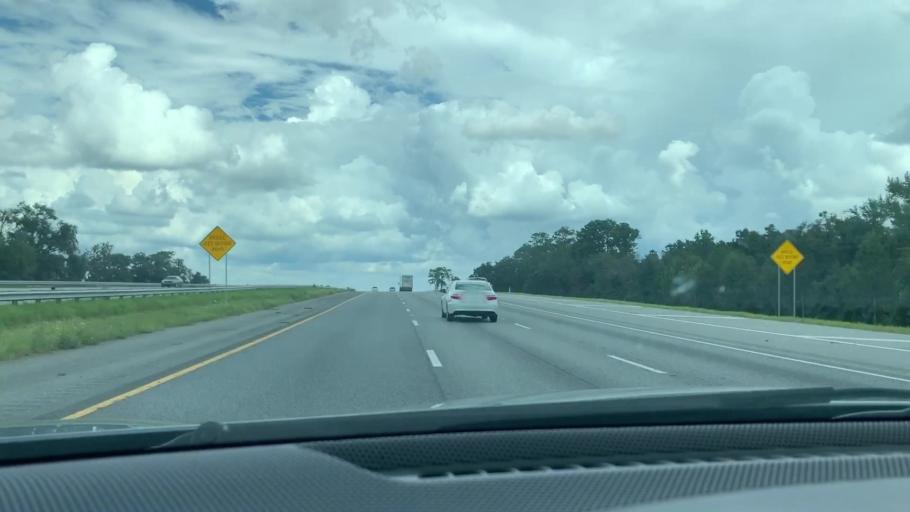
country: US
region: Georgia
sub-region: Glynn County
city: Dock Junction
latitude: 31.1633
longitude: -81.5558
